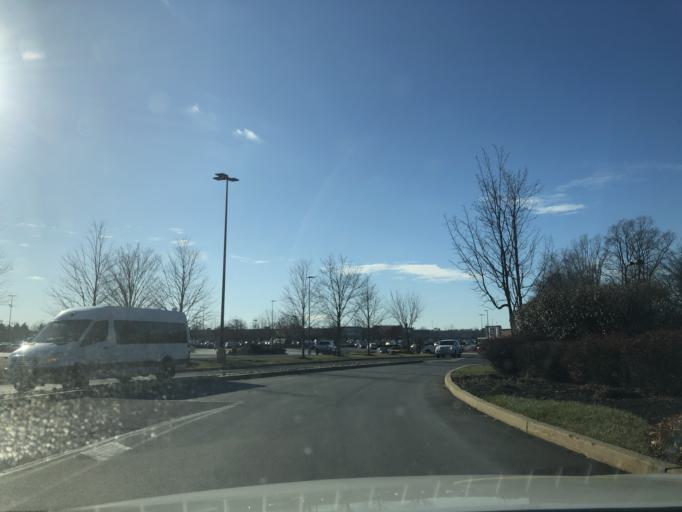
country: US
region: Pennsylvania
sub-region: Bucks County
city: Trevose
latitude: 40.1368
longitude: -74.9577
